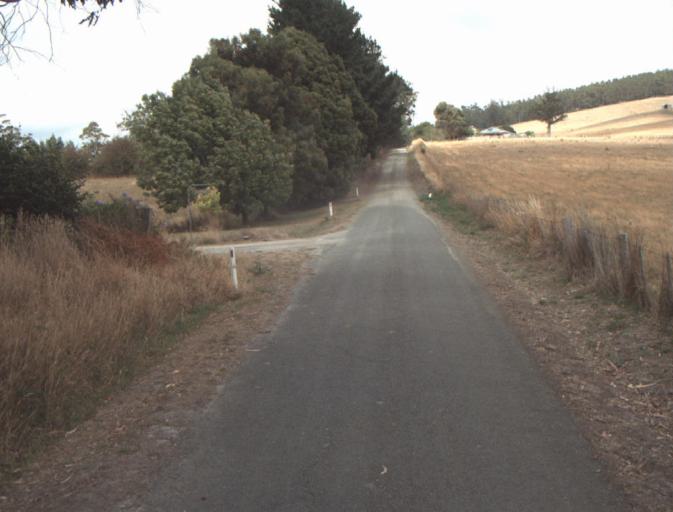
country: AU
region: Tasmania
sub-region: Launceston
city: Mayfield
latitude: -41.1705
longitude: 147.2130
